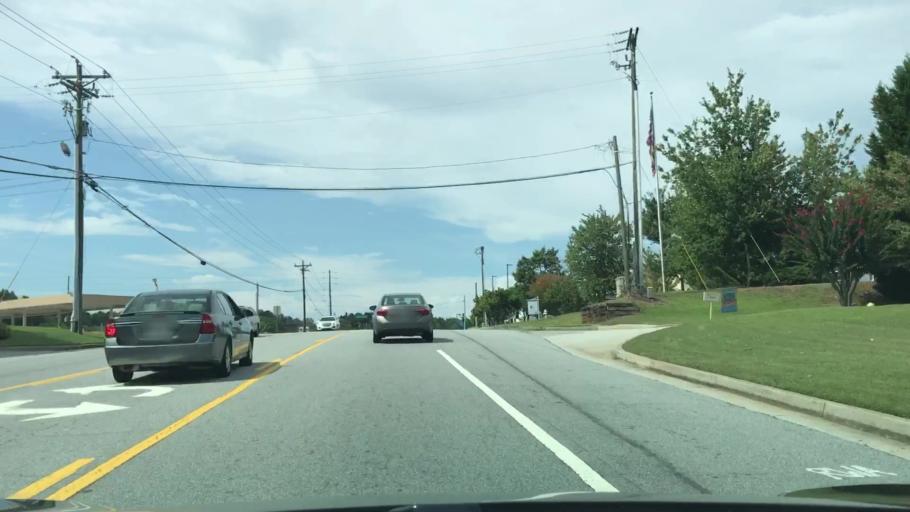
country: US
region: Georgia
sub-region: Gwinnett County
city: Snellville
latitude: 33.8854
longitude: -84.0592
